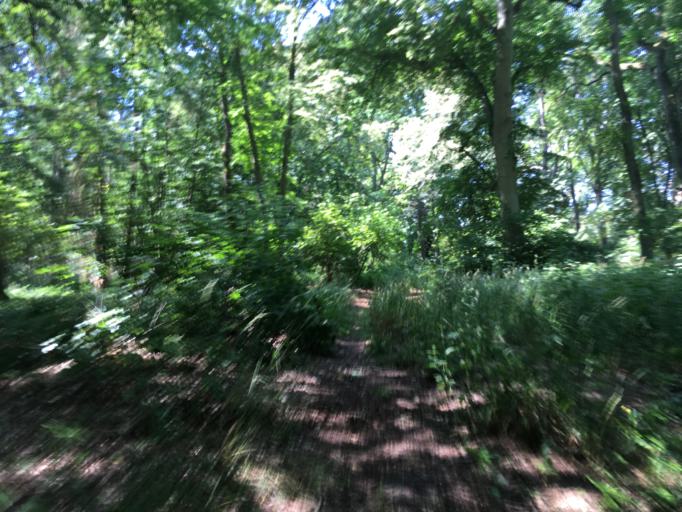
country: DE
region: Brandenburg
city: Zichow
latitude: 53.2341
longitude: 14.1066
